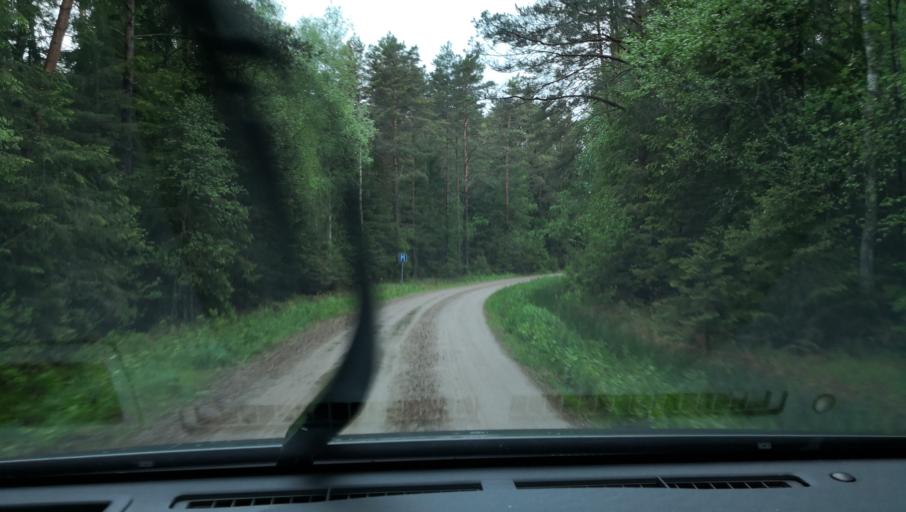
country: SE
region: Uppsala
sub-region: Enkopings Kommun
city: Orsundsbro
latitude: 59.9270
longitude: 17.3331
